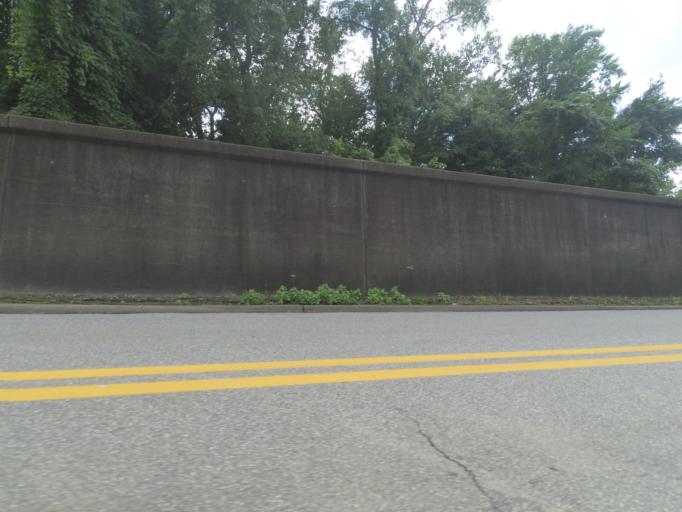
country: US
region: West Virginia
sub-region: Cabell County
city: Pea Ridge
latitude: 38.4136
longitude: -82.3652
